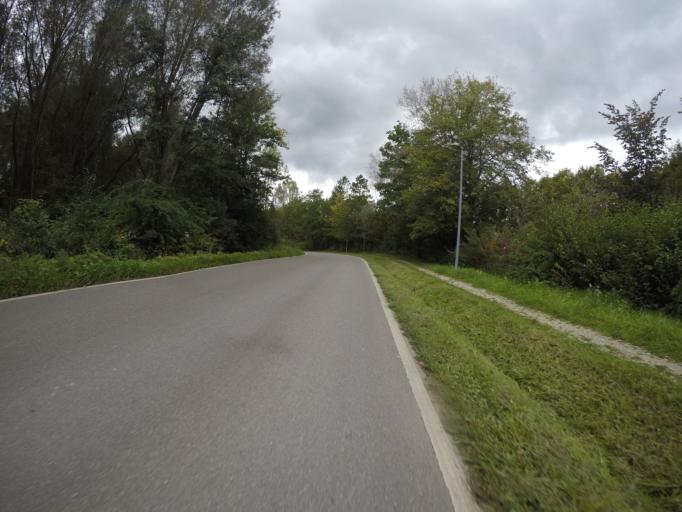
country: DE
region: Baden-Wuerttemberg
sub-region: Tuebingen Region
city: Reutlingen
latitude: 48.4776
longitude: 9.1850
